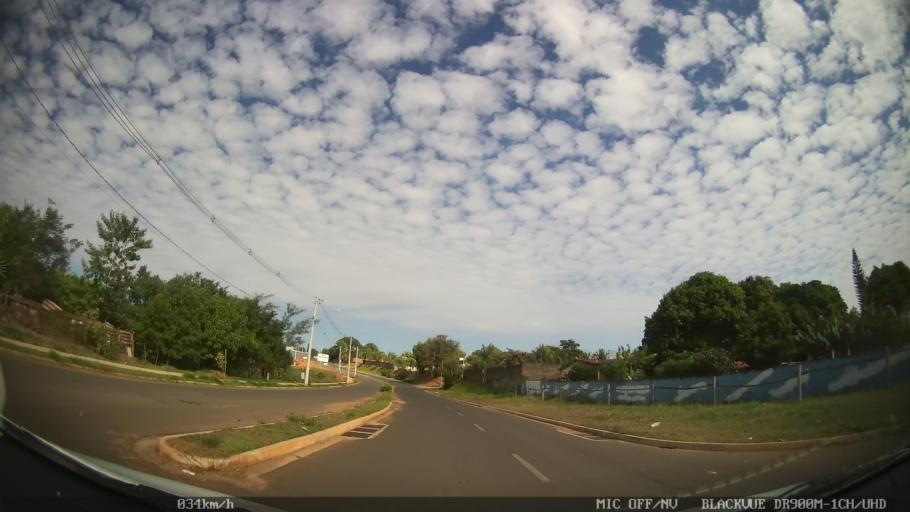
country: BR
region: Sao Paulo
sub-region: Santa Barbara D'Oeste
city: Santa Barbara d'Oeste
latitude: -22.7769
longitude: -47.4041
